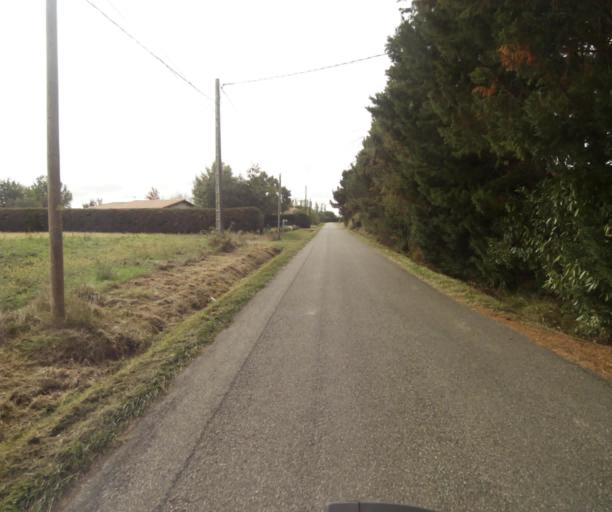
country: FR
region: Midi-Pyrenees
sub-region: Departement du Tarn-et-Garonne
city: Finhan
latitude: 43.9235
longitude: 1.2454
